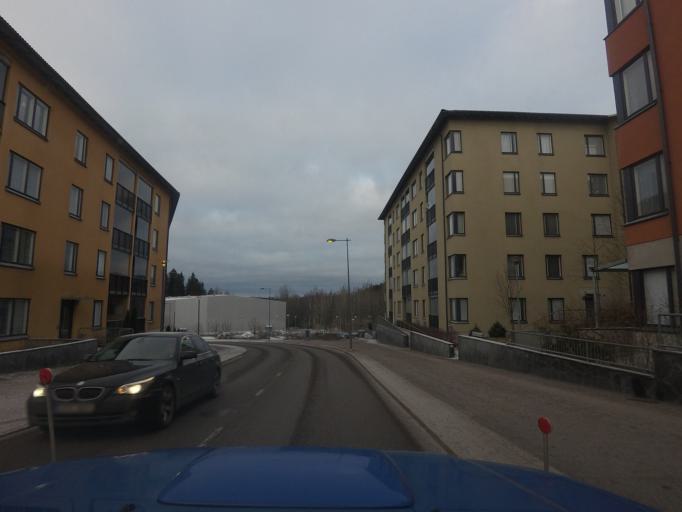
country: FI
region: Uusimaa
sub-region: Helsinki
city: Espoo
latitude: 60.2087
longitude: 24.6797
